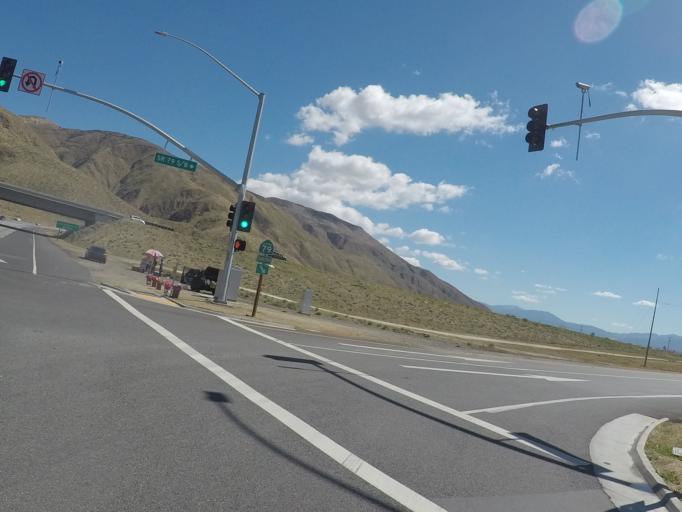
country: US
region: California
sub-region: Riverside County
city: San Jacinto
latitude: 33.8454
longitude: -117.0055
